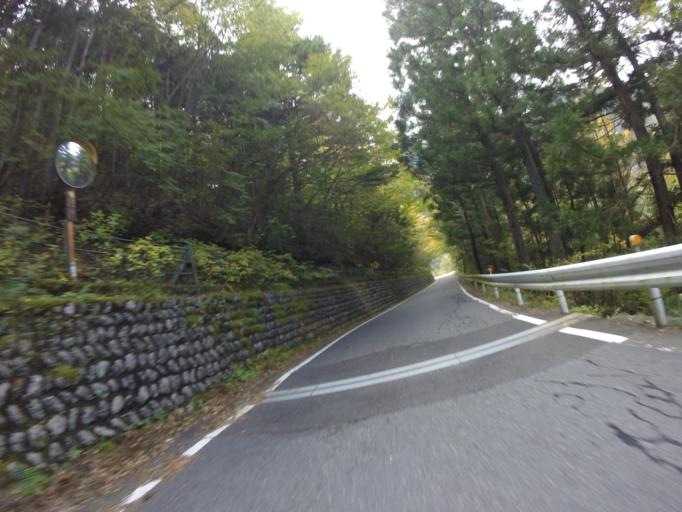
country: JP
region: Shizuoka
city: Shizuoka-shi
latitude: 35.1608
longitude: 138.1347
